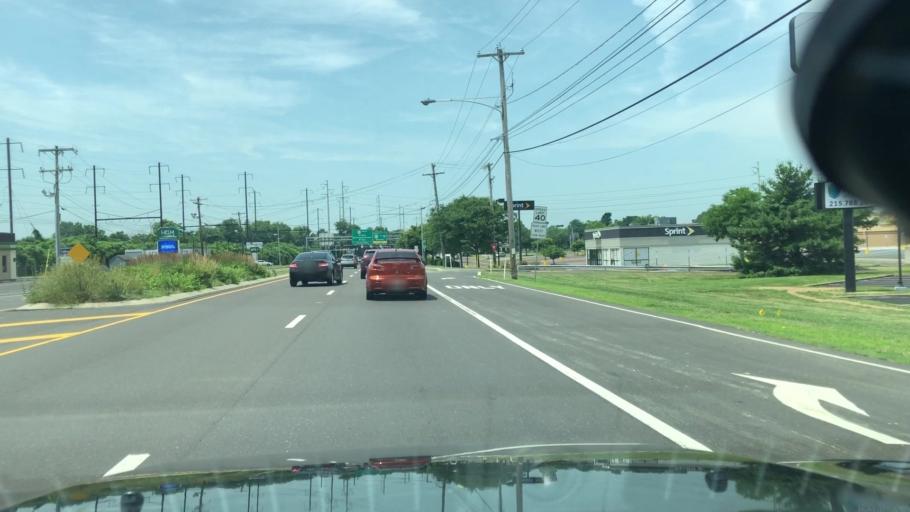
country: US
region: Pennsylvania
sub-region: Bucks County
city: Bristol
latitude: 40.0999
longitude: -74.8696
